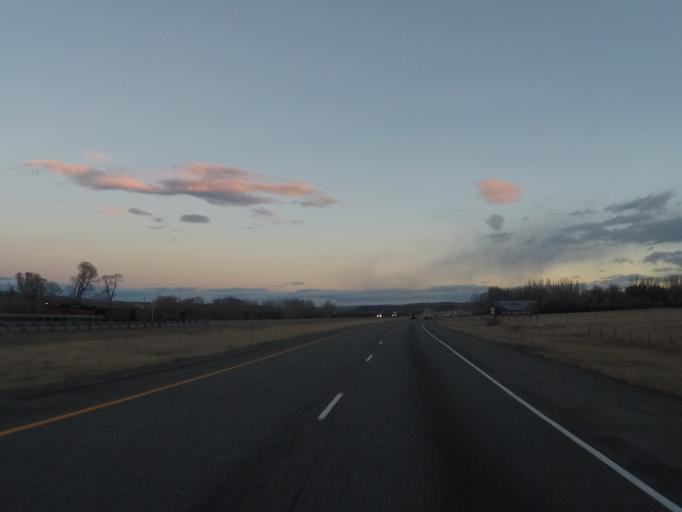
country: US
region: Montana
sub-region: Sweet Grass County
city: Big Timber
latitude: 45.7785
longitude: -109.8031
